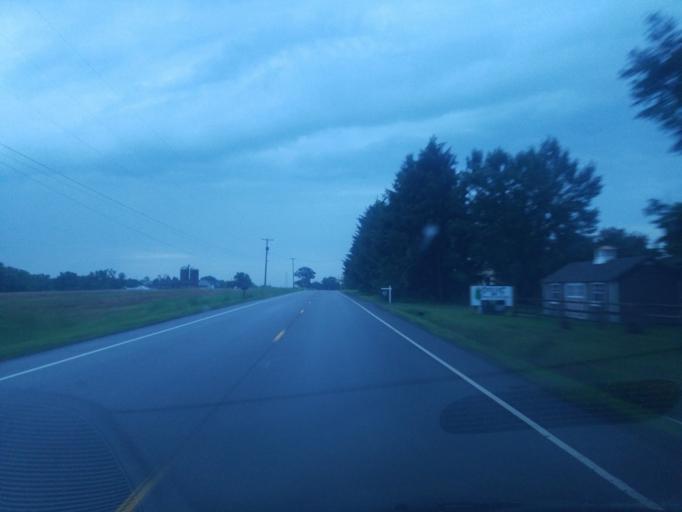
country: US
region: Ohio
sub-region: Mahoning County
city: Canfield
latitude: 40.9849
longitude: -80.7581
